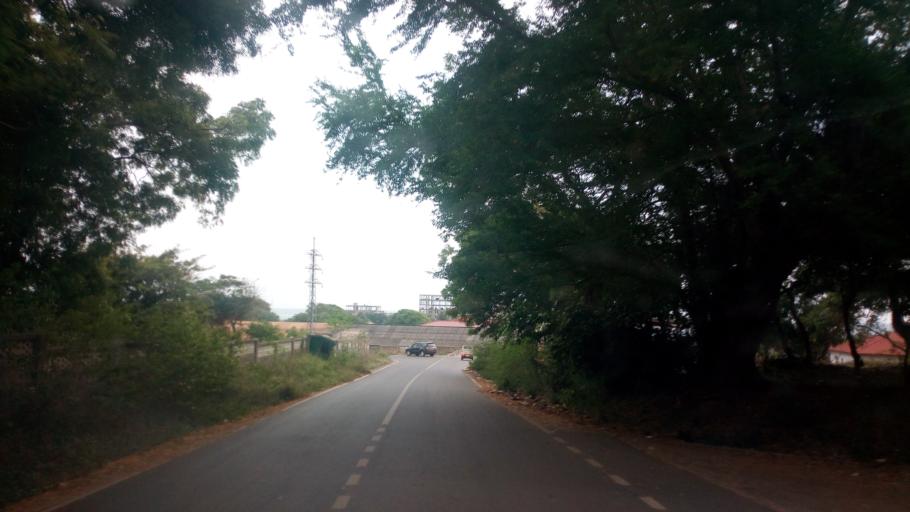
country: GH
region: Western
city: Takoradi
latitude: 4.8802
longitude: -1.7615
